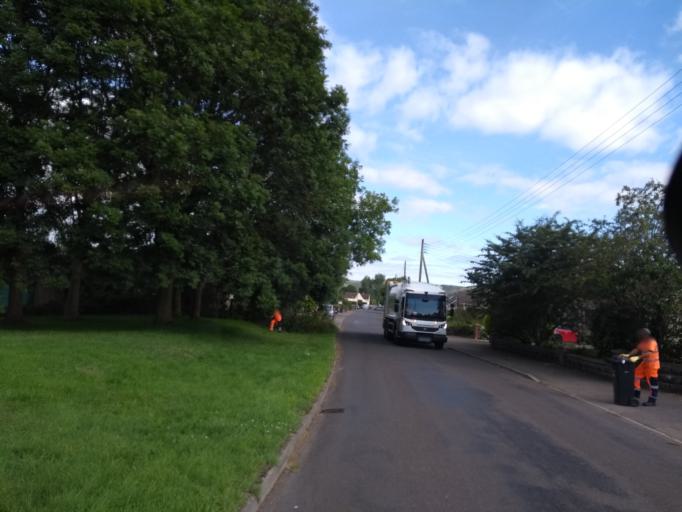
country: GB
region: England
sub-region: Somerset
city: Axbridge
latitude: 51.2768
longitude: -2.8513
